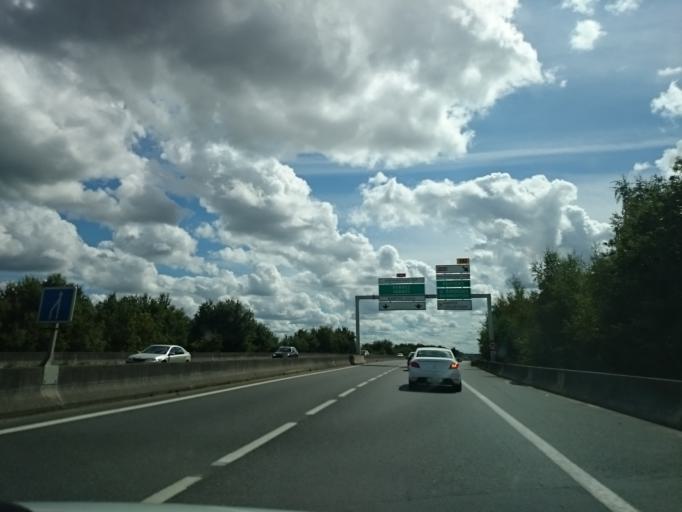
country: FR
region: Pays de la Loire
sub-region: Departement de la Loire-Atlantique
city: Sainte-Luce-sur-Loire
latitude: 47.2439
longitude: -1.4758
